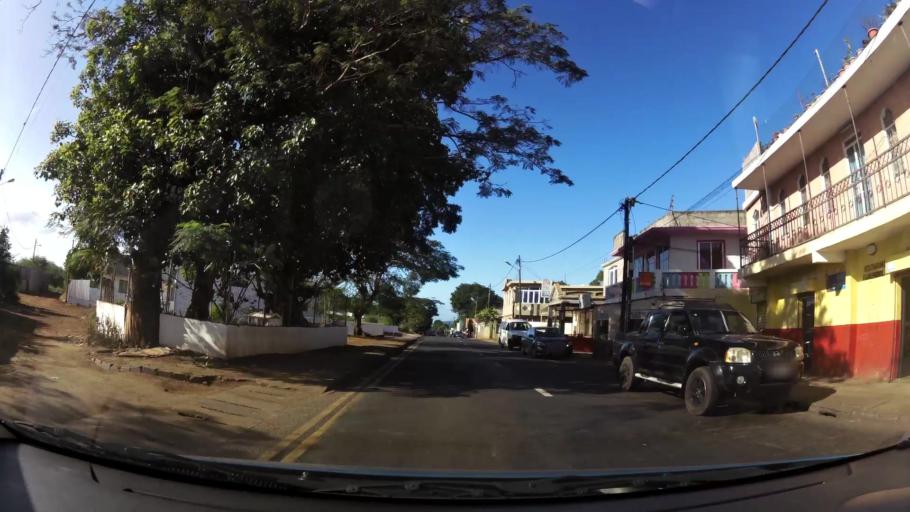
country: MU
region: Black River
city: Petite Riviere
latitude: -20.1904
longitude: 57.4542
